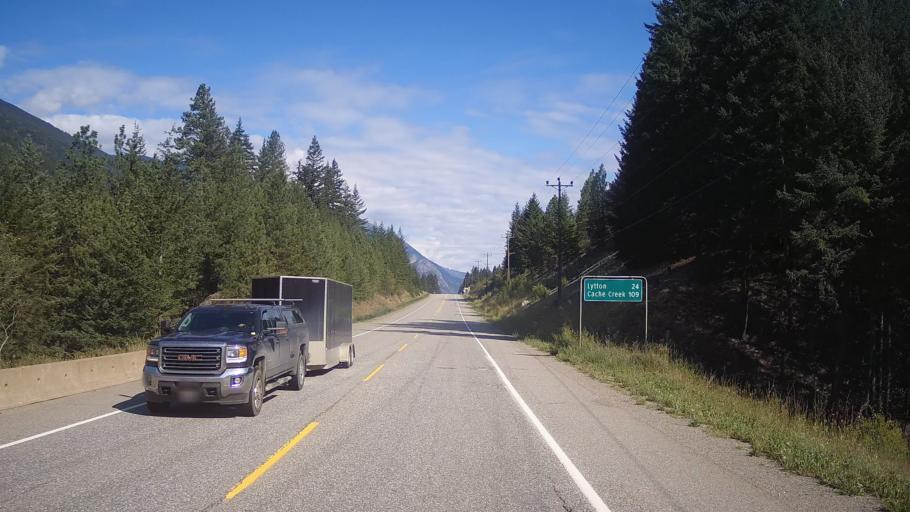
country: CA
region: British Columbia
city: Hope
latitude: 50.0319
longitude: -121.5307
